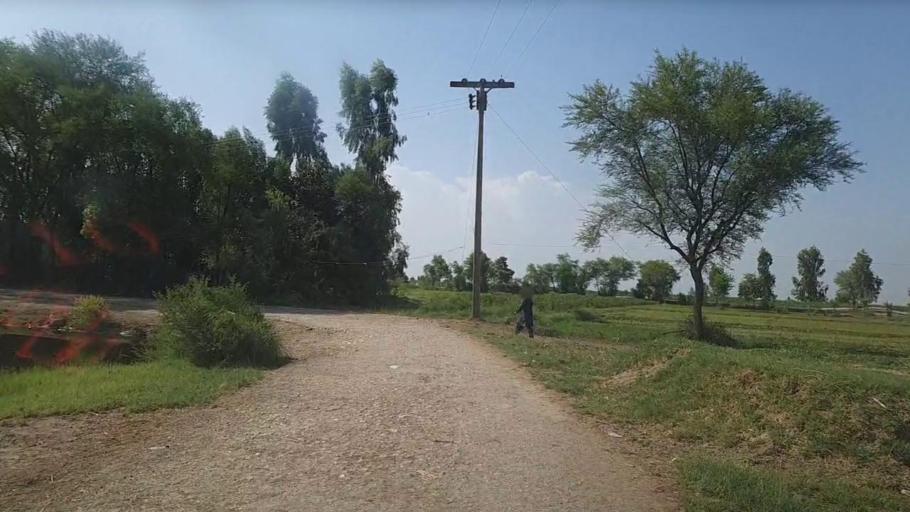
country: PK
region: Sindh
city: Mirpur Mathelo
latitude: 28.1163
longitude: 69.5890
